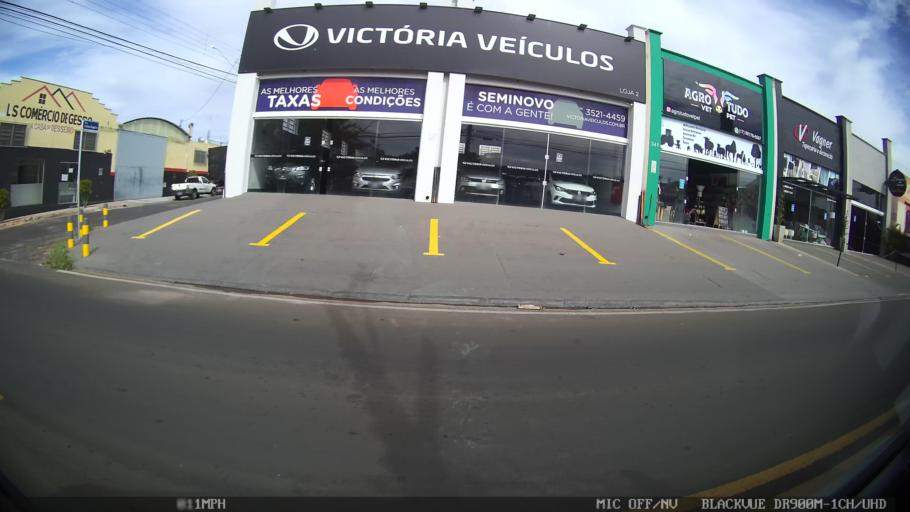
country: BR
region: Sao Paulo
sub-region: Catanduva
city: Catanduva
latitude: -21.1477
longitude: -48.9633
